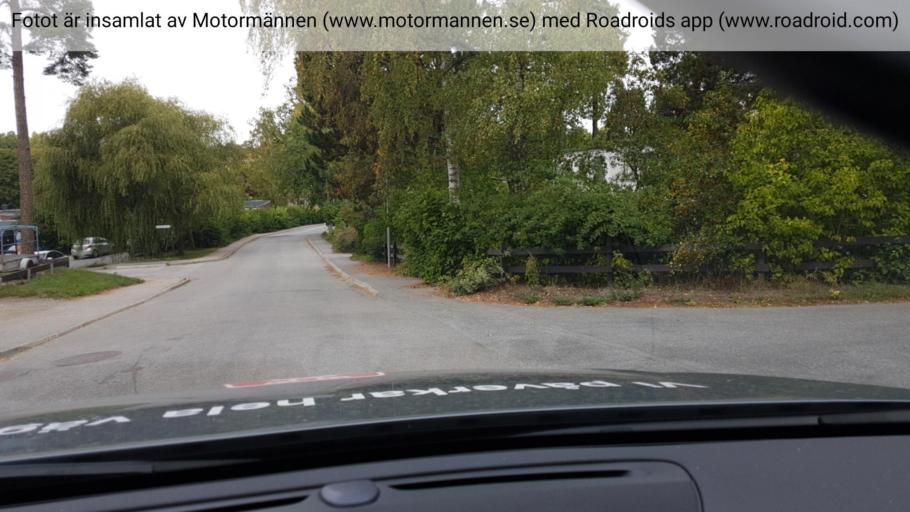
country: SE
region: Stockholm
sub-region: Danderyds Kommun
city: Djursholm
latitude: 59.3833
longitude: 18.0626
